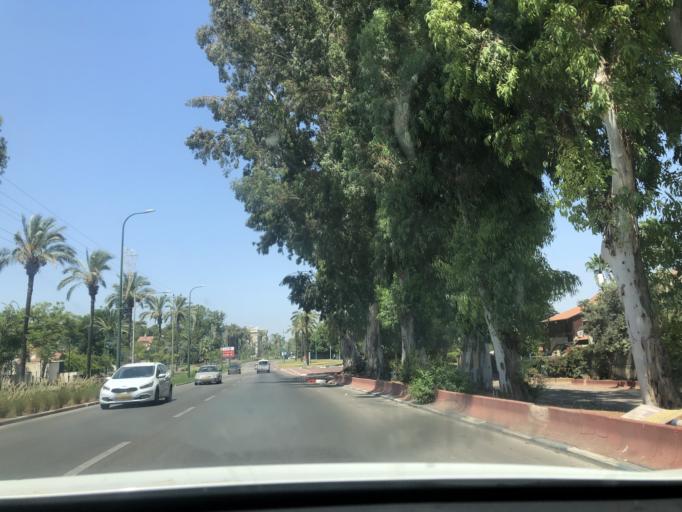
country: IL
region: Central District
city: Lod
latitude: 31.9404
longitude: 34.8873
